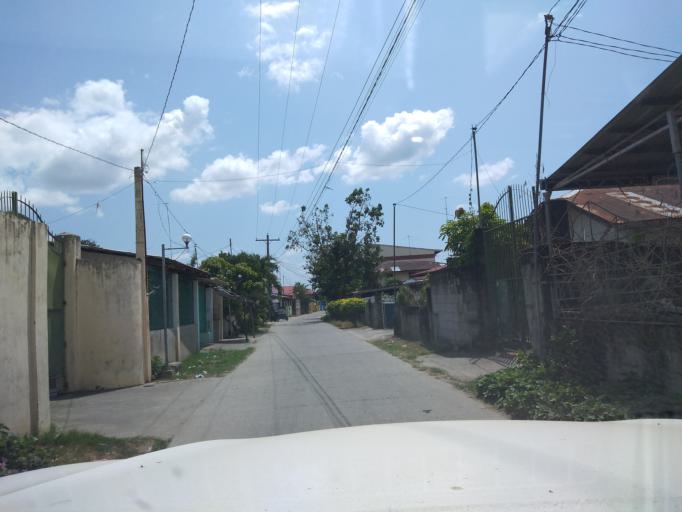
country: PH
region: Central Luzon
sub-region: Province of Pampanga
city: Bahay Pare
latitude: 15.0163
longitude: 120.8714
